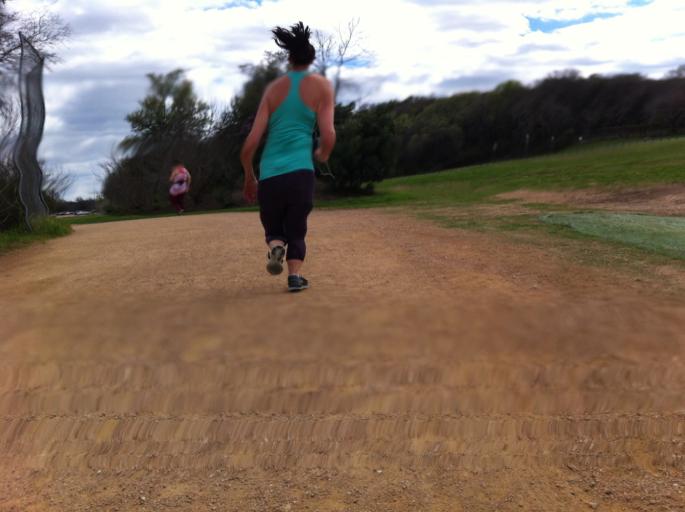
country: US
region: Texas
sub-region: Travis County
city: Rollingwood
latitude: 30.2724
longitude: -97.7719
